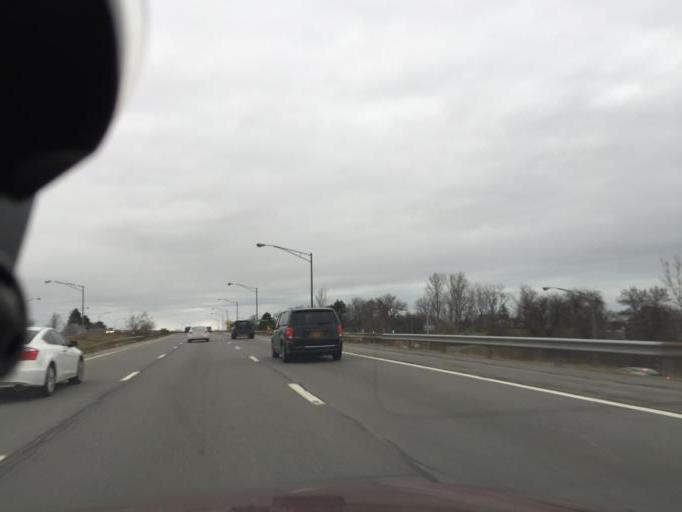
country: US
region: New York
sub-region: Monroe County
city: North Gates
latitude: 43.1775
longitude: -77.6833
